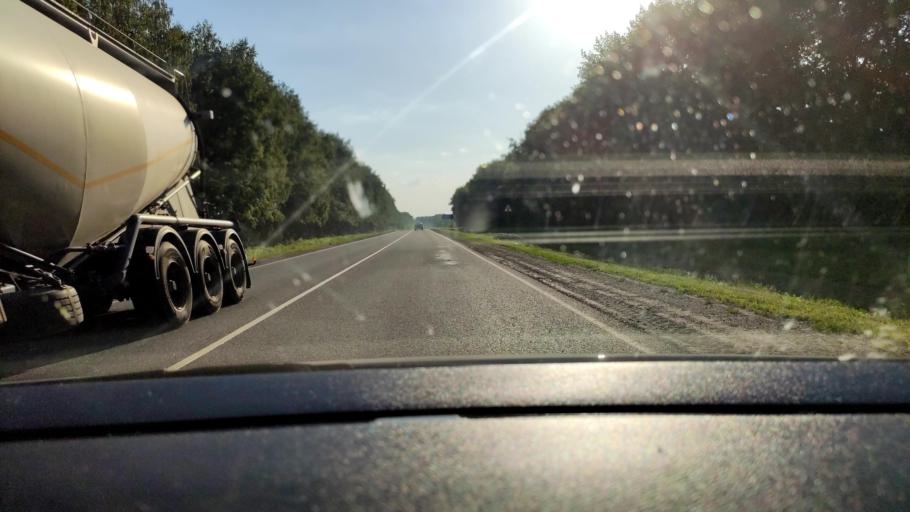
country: RU
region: Voronezj
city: Kashirskoye
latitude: 51.4589
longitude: 39.7893
